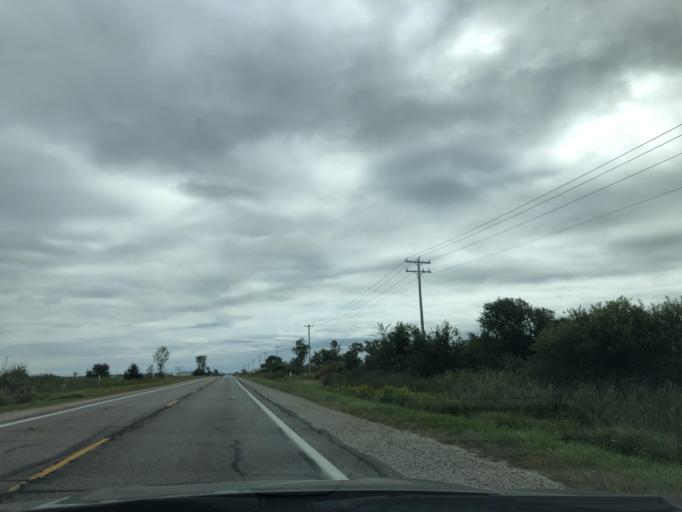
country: US
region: Michigan
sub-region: Missaukee County
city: Lake City
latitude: 44.1936
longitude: -85.1773
